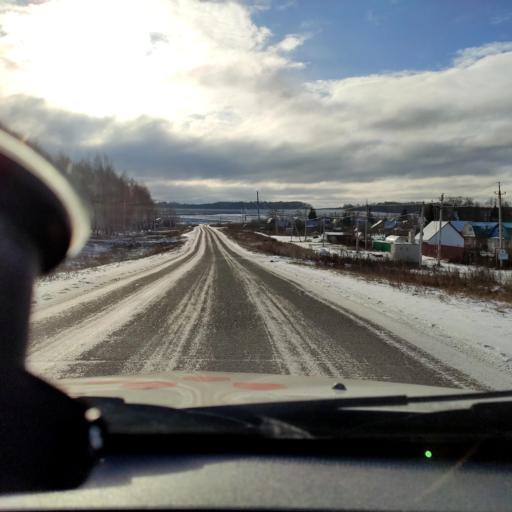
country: RU
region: Bashkortostan
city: Mikhaylovka
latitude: 54.8028
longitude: 55.7792
